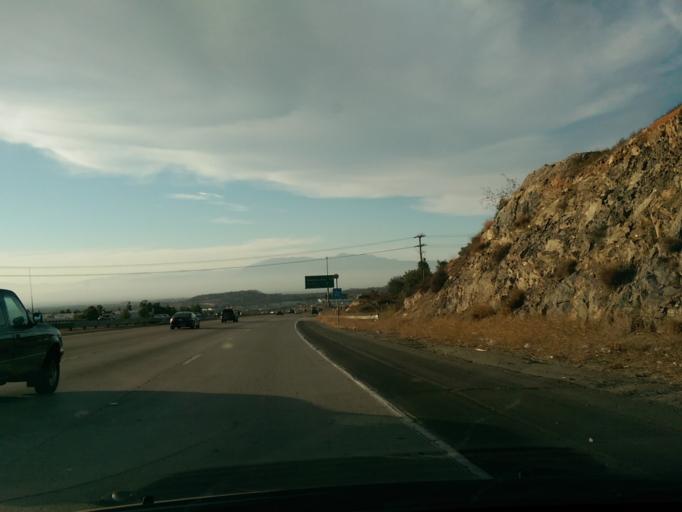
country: US
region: California
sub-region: Riverside County
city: El Cerrito
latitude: 33.8530
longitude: -117.5349
